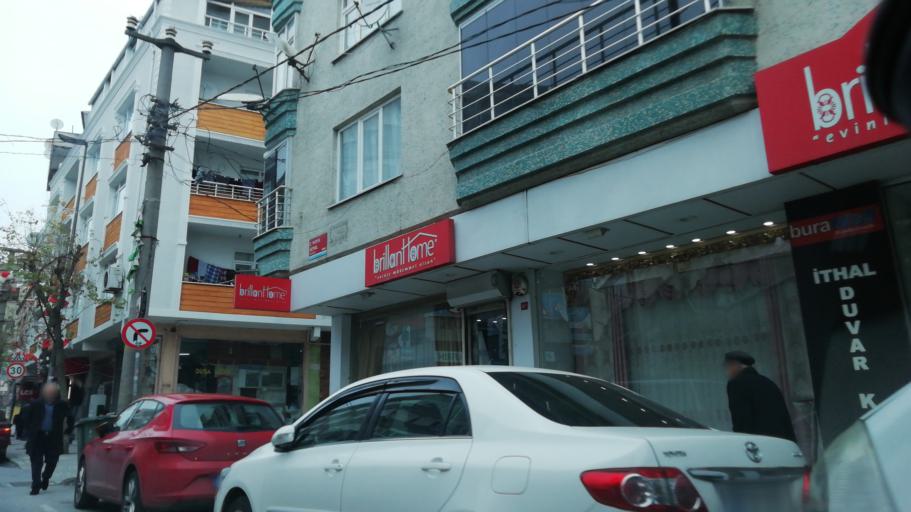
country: TR
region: Istanbul
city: Mahmutbey
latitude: 41.0022
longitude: 28.7995
